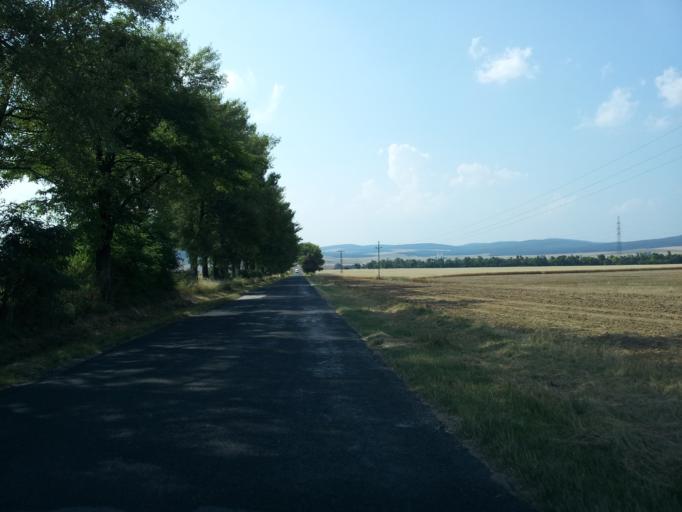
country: HU
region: Veszprem
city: Nemesvamos
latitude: 47.0197
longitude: 17.8050
